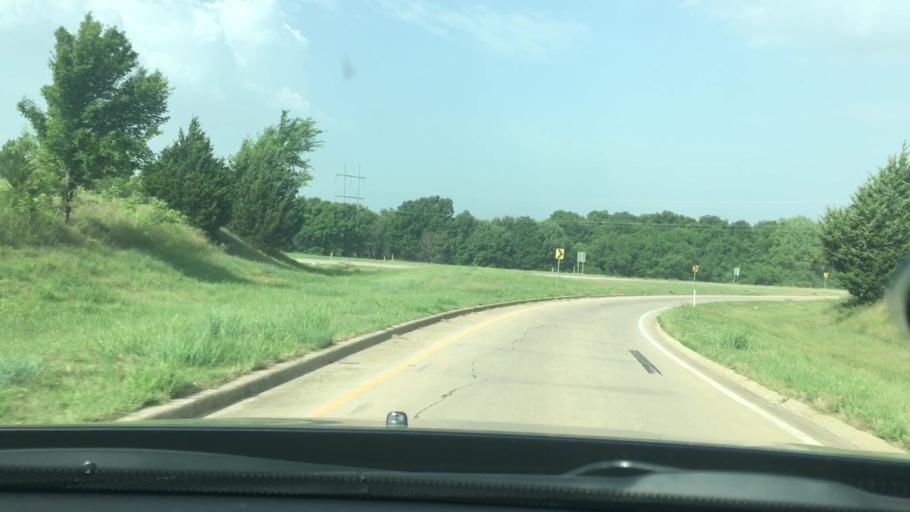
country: US
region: Oklahoma
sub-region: Pontotoc County
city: Ada
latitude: 34.7777
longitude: -96.7036
